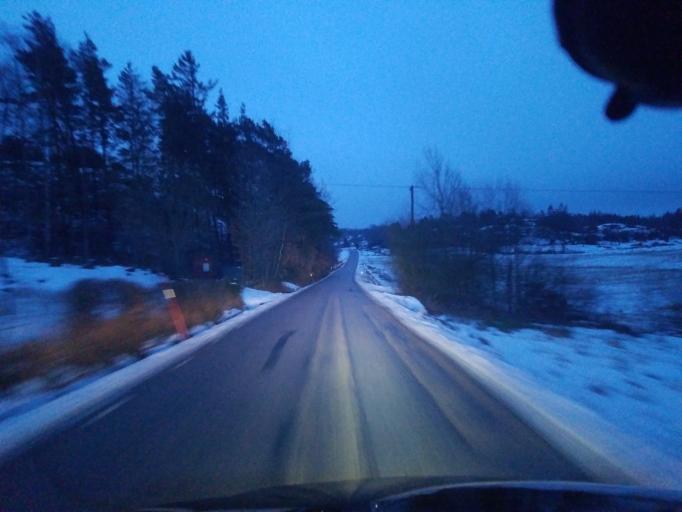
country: SE
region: Vaestra Goetaland
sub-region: Orust
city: Henan
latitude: 58.2840
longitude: 11.5827
